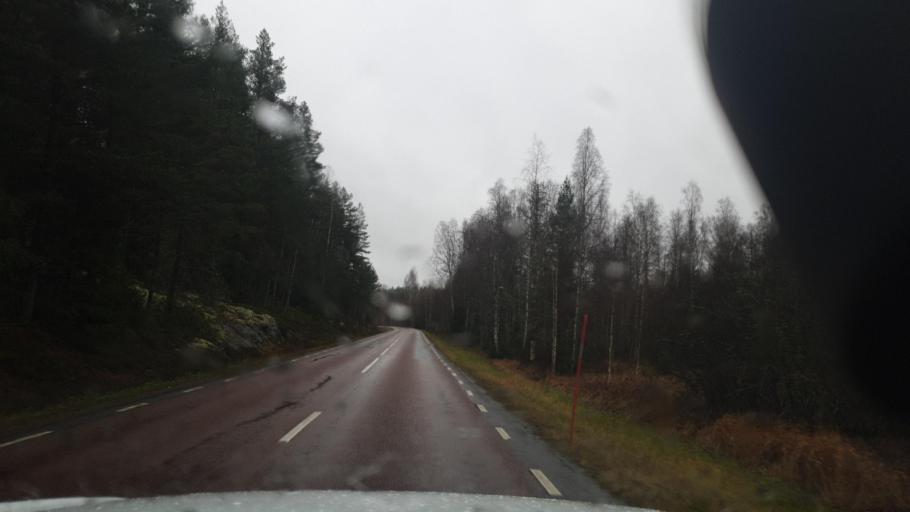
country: SE
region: Vaermland
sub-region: Grums Kommun
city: Grums
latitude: 59.4425
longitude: 12.9769
